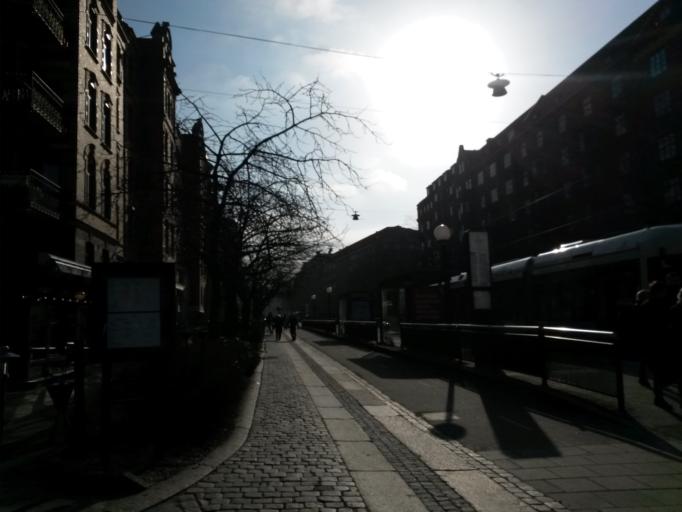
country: SE
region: Vaestra Goetaland
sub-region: Goteborg
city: Goeteborg
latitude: 57.6985
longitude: 11.9823
